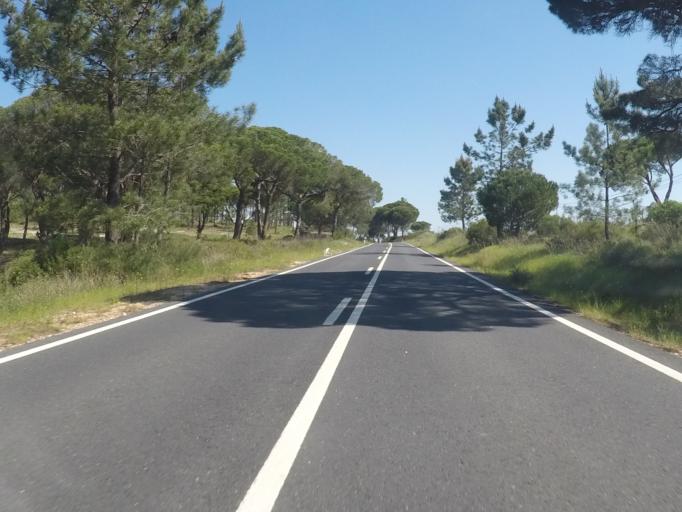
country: PT
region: Setubal
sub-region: Grandola
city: Grandola
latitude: 38.2775
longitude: -8.7260
